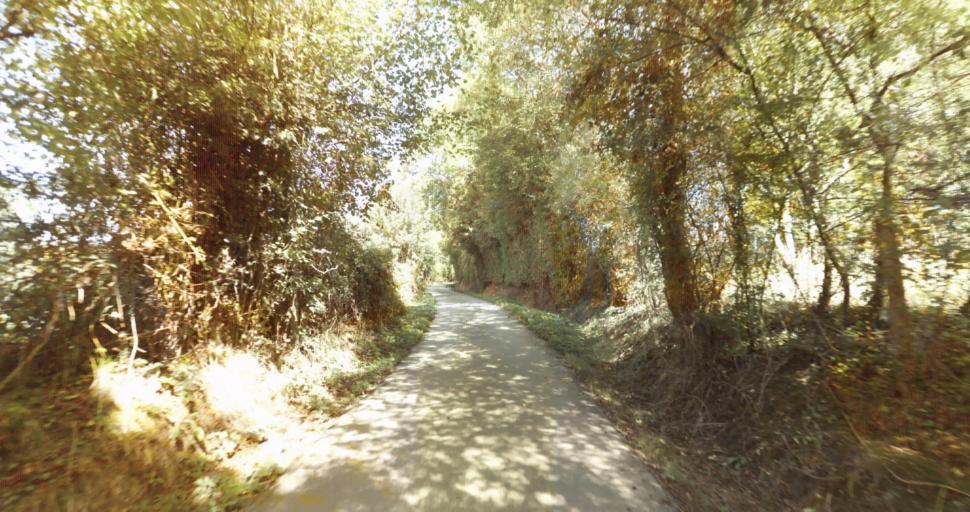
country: FR
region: Lower Normandy
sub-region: Departement de l'Orne
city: Gace
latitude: 48.7259
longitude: 0.2419
